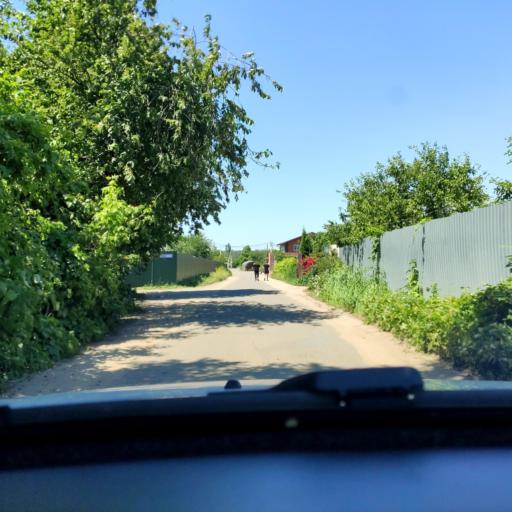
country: RU
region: Voronezj
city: Shilovo
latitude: 51.5891
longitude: 39.1524
